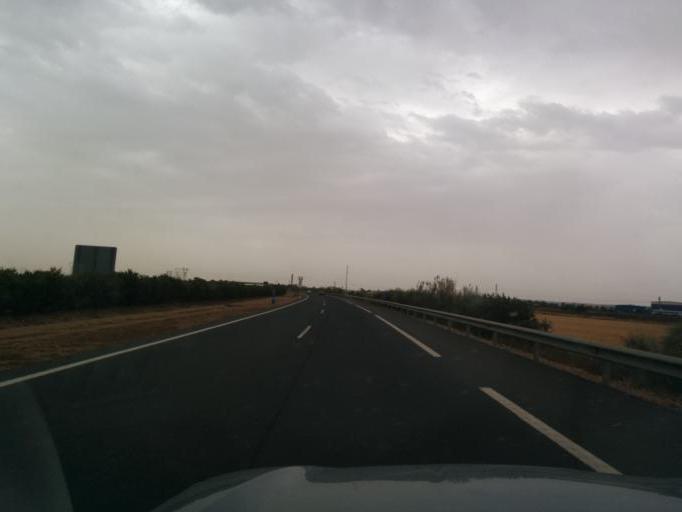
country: ES
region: Andalusia
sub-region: Provincia de Huelva
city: San Juan del Puerto
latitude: 37.3146
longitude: -6.8954
